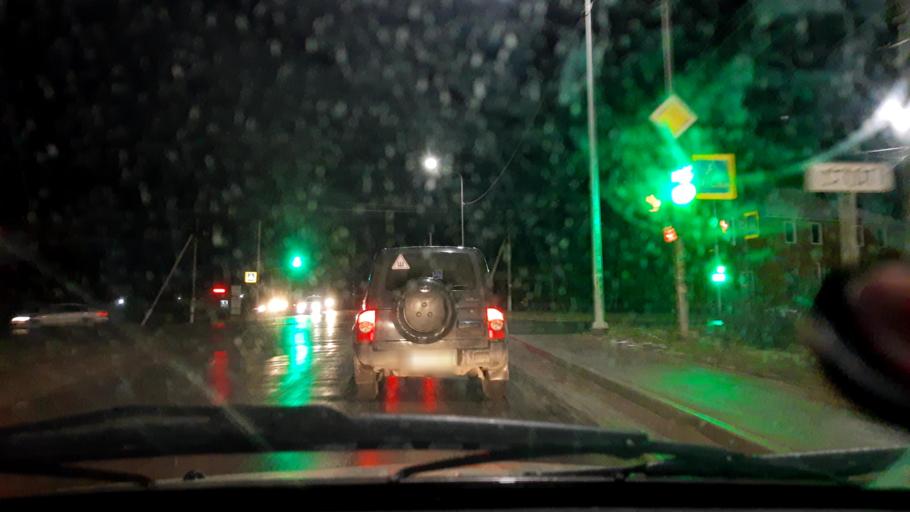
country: RU
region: Bashkortostan
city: Mikhaylovka
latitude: 54.8139
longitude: 55.8854
